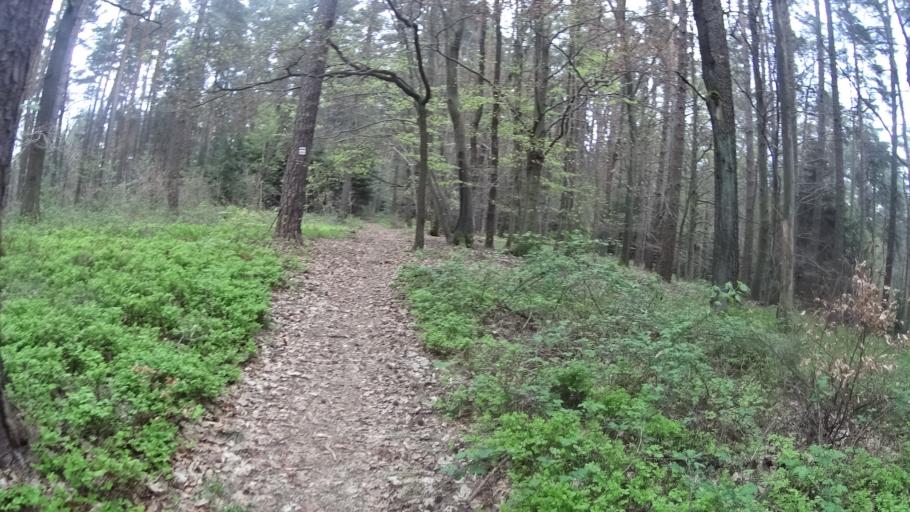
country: DE
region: Bavaria
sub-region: Upper Franconia
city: Kleinsendelbach
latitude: 49.6181
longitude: 11.1804
